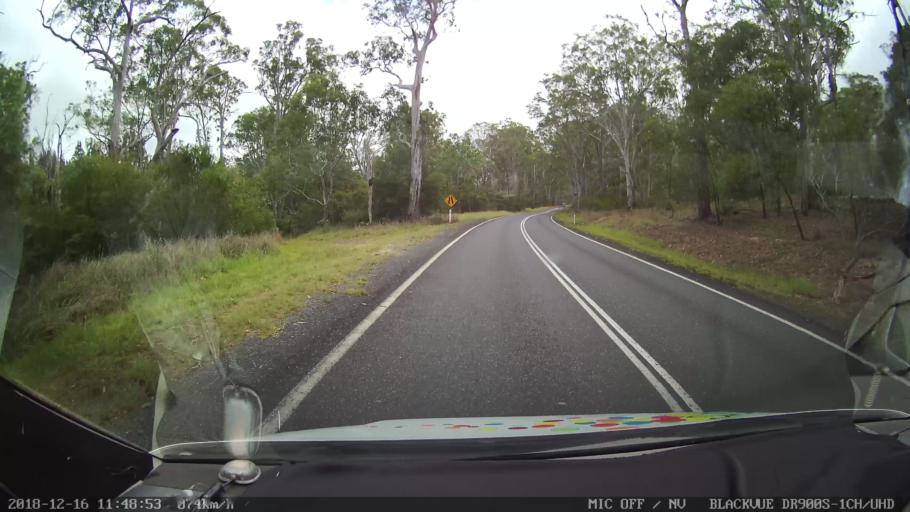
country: AU
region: New South Wales
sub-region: Tenterfield Municipality
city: Carrolls Creek
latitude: -28.9180
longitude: 152.2506
